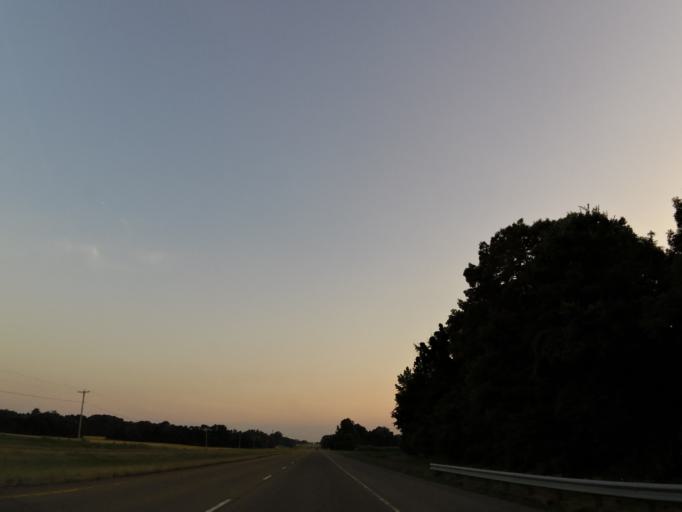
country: US
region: Tennessee
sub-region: Carroll County
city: McKenzie
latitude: 36.1817
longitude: -88.4384
